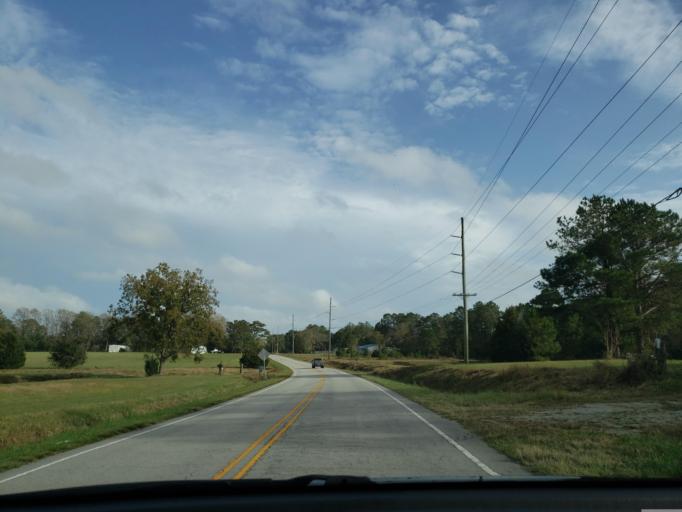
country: US
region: North Carolina
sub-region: Onslow County
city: Jacksonville
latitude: 34.6892
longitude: -77.5393
